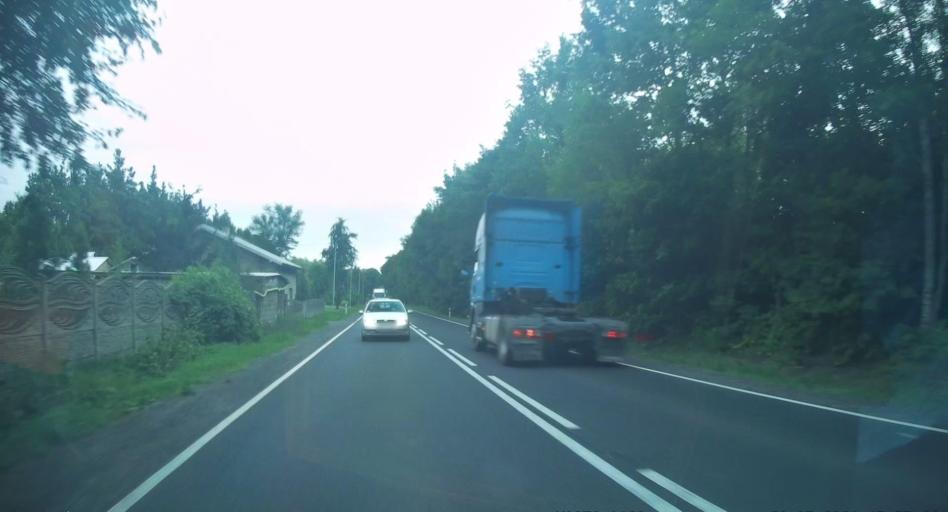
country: PL
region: Lodz Voivodeship
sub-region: Powiat radomszczanski
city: Gomunice
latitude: 51.1755
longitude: 19.4947
